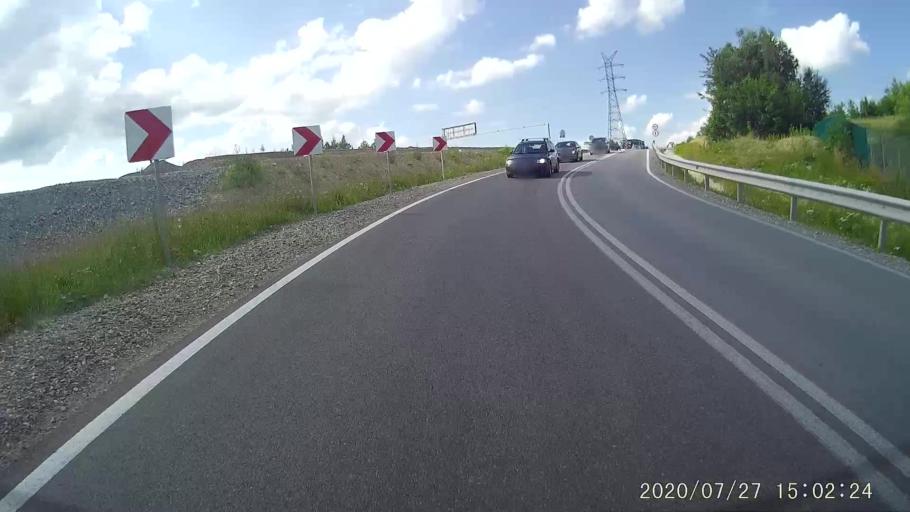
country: PL
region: Lesser Poland Voivodeship
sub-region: Powiat suski
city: Naprawa
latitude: 49.6729
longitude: 19.8883
